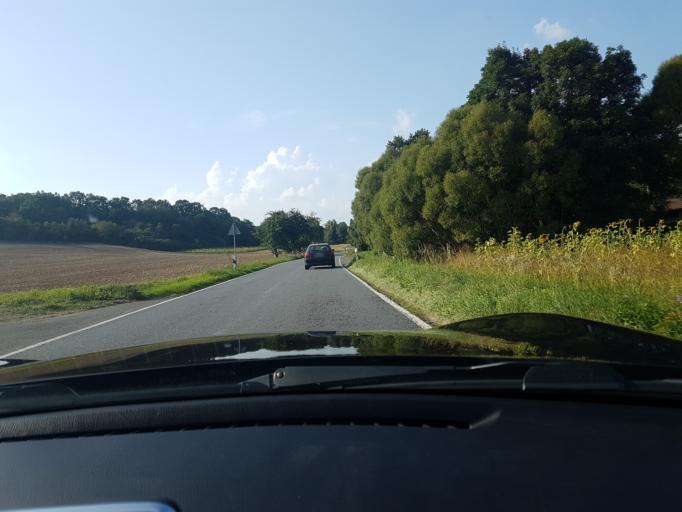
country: DE
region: Baden-Wuerttemberg
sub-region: Karlsruhe Region
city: Seckach
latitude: 49.4479
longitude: 9.3691
